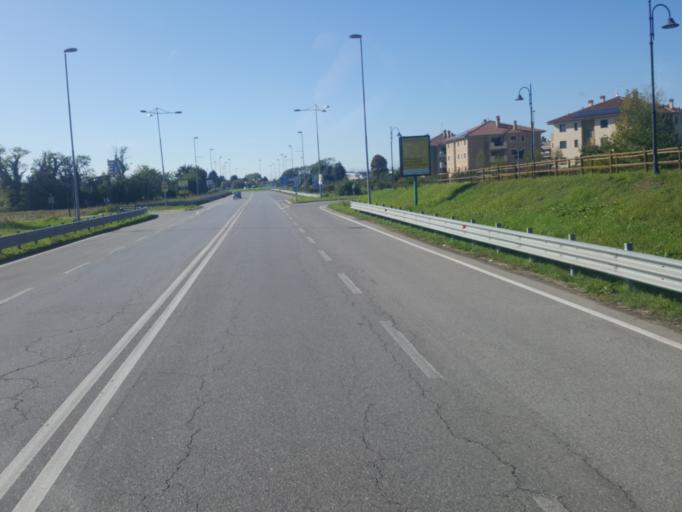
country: IT
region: Lombardy
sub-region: Citta metropolitana di Milano
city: Vittuone
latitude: 45.4819
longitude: 8.9539
